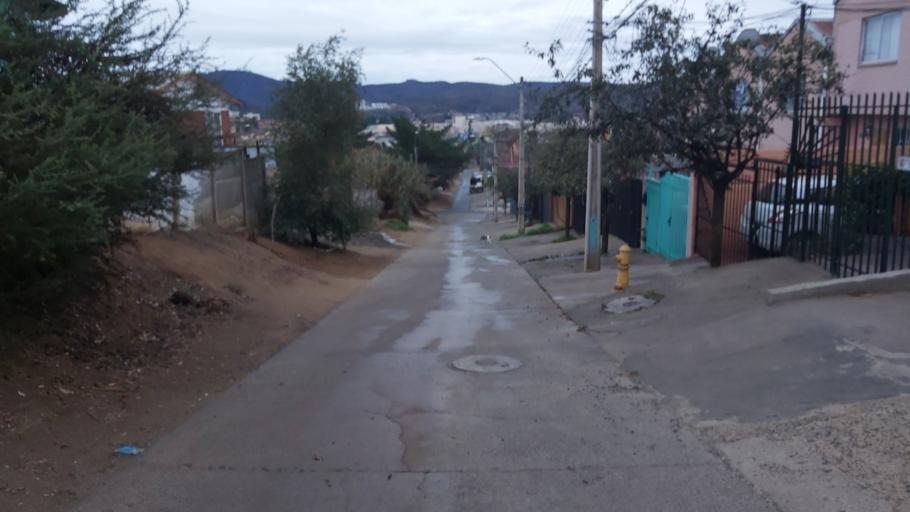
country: CL
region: Valparaiso
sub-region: Provincia de Marga Marga
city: Quilpue
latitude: -33.0526
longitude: -71.4218
